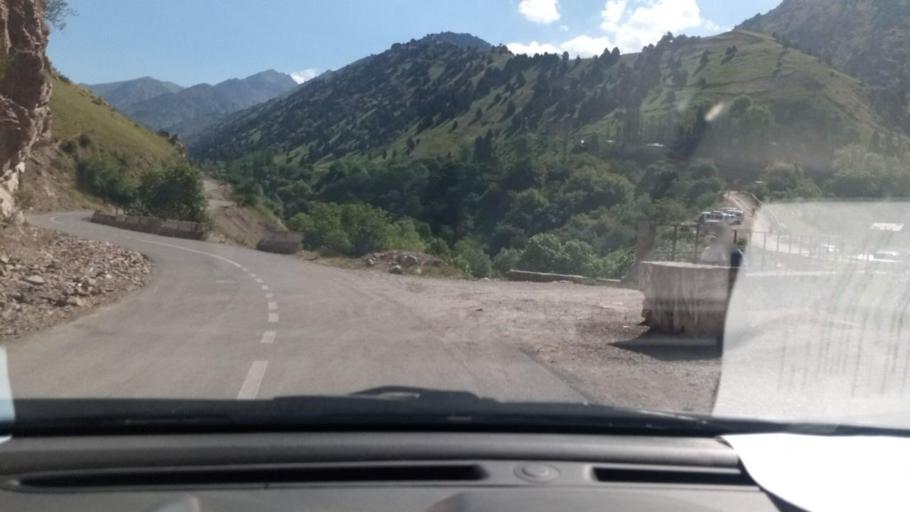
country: UZ
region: Toshkent
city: Yangiobod
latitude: 41.1240
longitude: 70.1050
